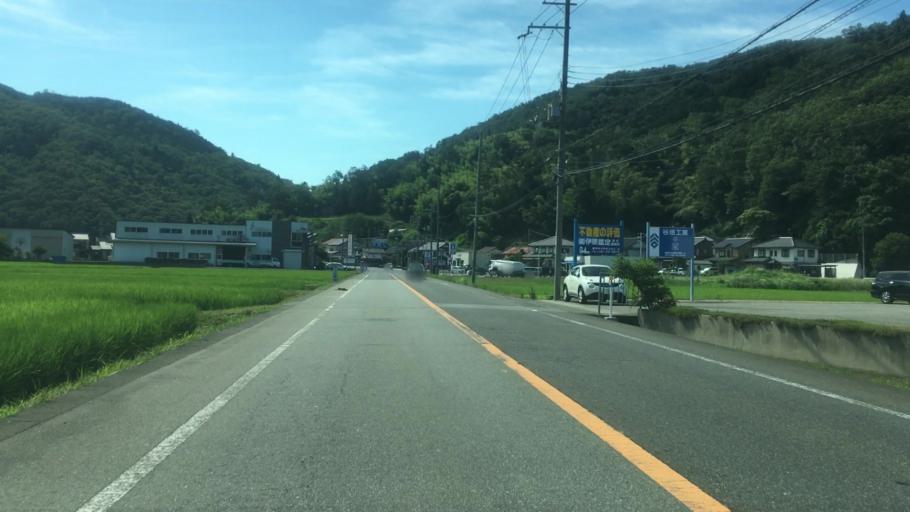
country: JP
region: Hyogo
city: Toyooka
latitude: 35.5660
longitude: 134.7897
